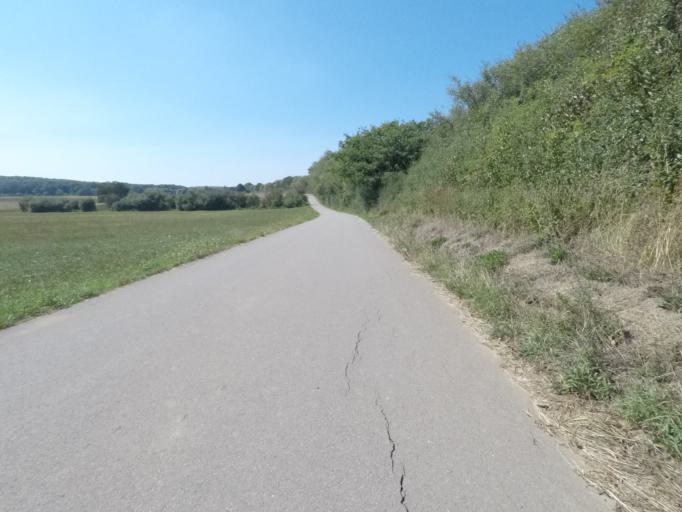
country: LU
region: Luxembourg
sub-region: Canton de Capellen
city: Steinfort
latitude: 49.6333
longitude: 5.9053
